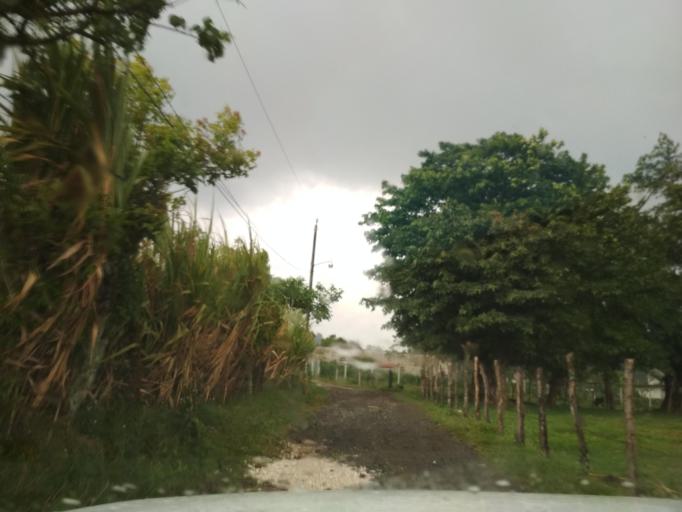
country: MX
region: Veracruz
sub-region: Mariano Escobedo
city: Chicola
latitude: 18.9046
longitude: -97.1167
